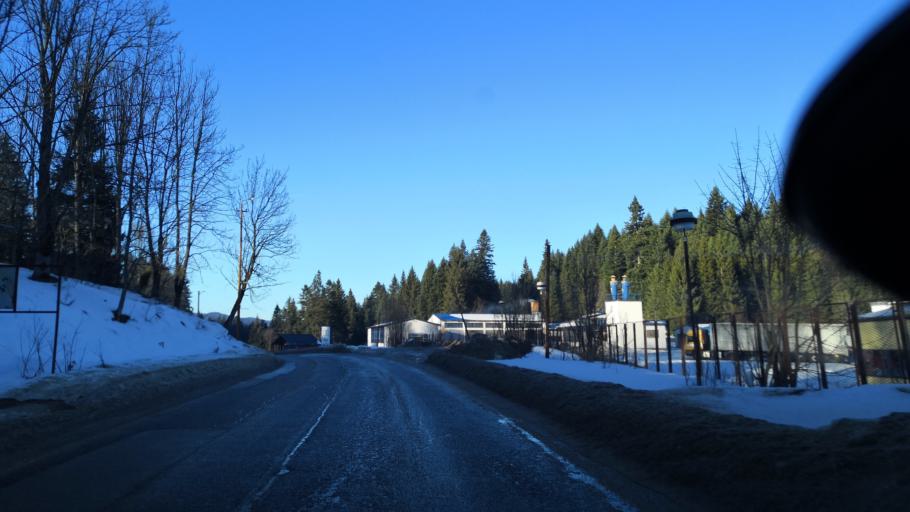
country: BA
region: Republika Srpska
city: Han Pijesak
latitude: 44.0840
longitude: 18.9545
